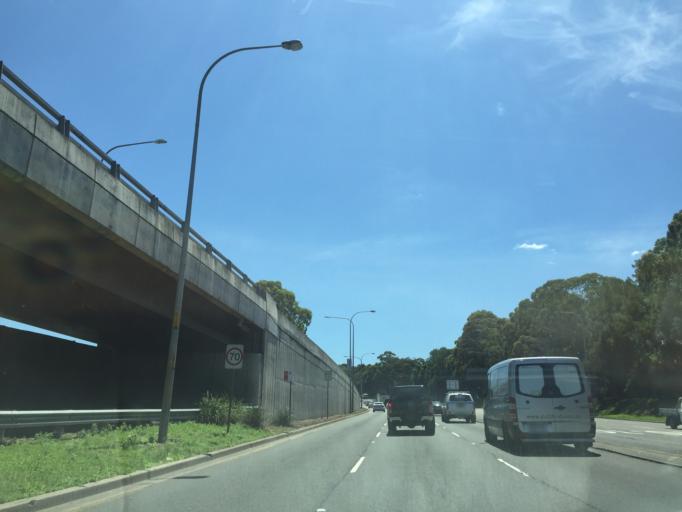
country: AU
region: New South Wales
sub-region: Parramatta
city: Constitution Hill
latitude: -33.7941
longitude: 150.9829
